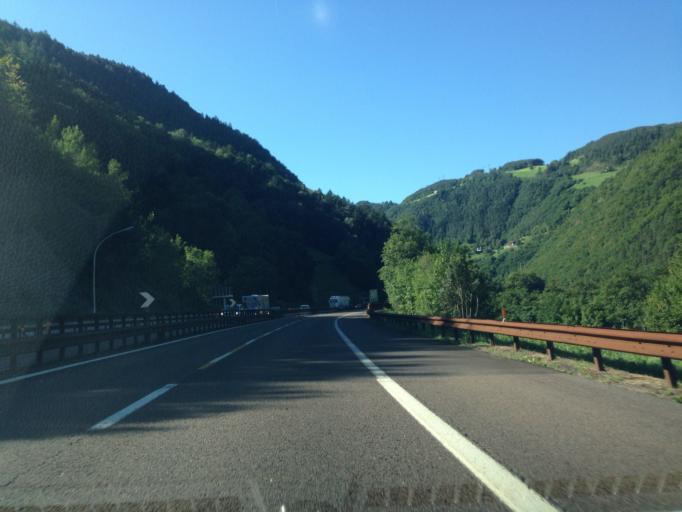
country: IT
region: Trentino-Alto Adige
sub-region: Bolzano
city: Ponte Gardena
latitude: 46.5679
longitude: 11.5217
